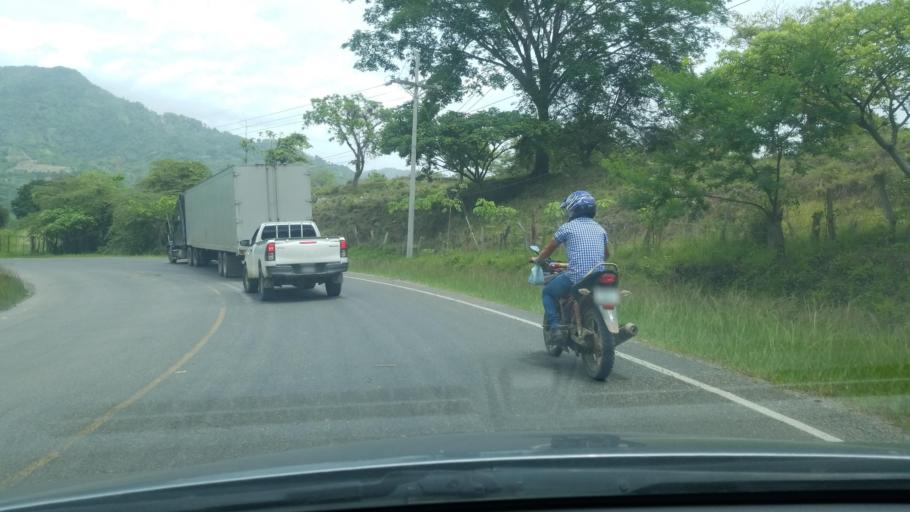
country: HN
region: Copan
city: Santa Rosa de Copan
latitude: 14.7253
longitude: -88.7698
